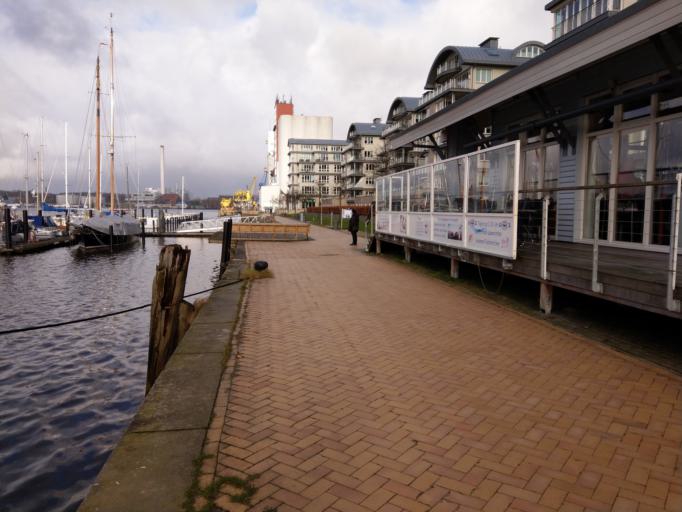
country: DE
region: Schleswig-Holstein
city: Flensburg
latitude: 54.7939
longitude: 9.4375
